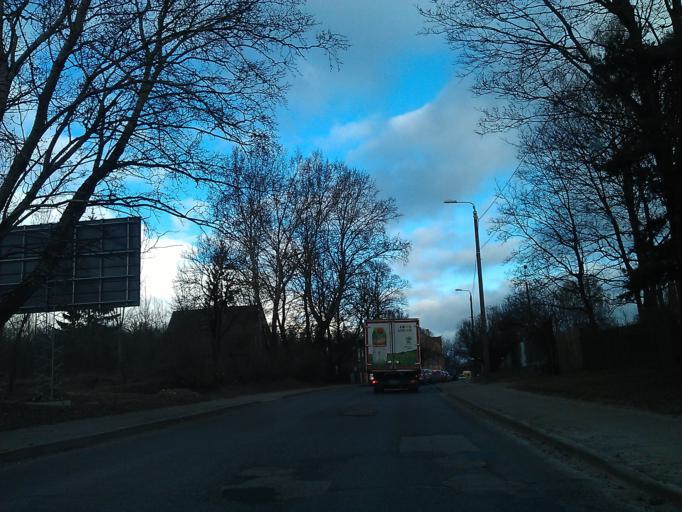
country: LV
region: Kekava
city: Balozi
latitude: 56.9125
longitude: 24.1434
